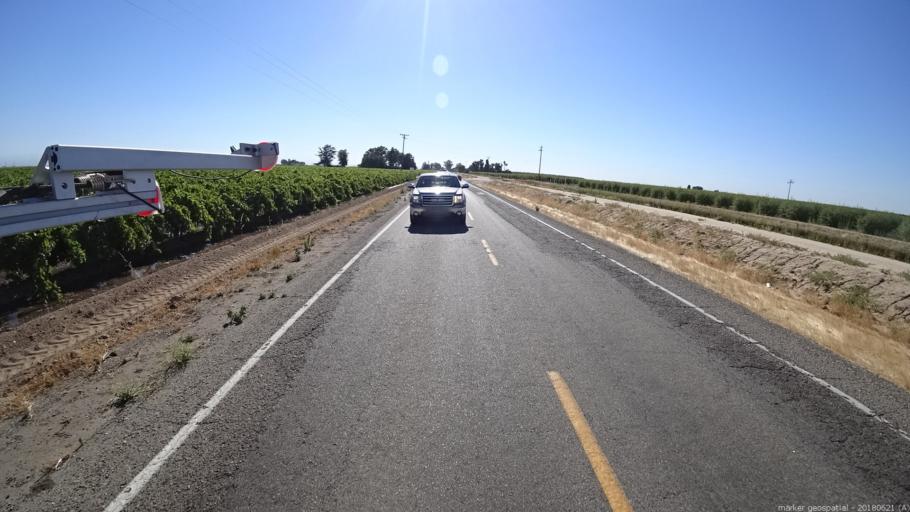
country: US
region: California
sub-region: Fresno County
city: Biola
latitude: 36.8513
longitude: -119.9934
